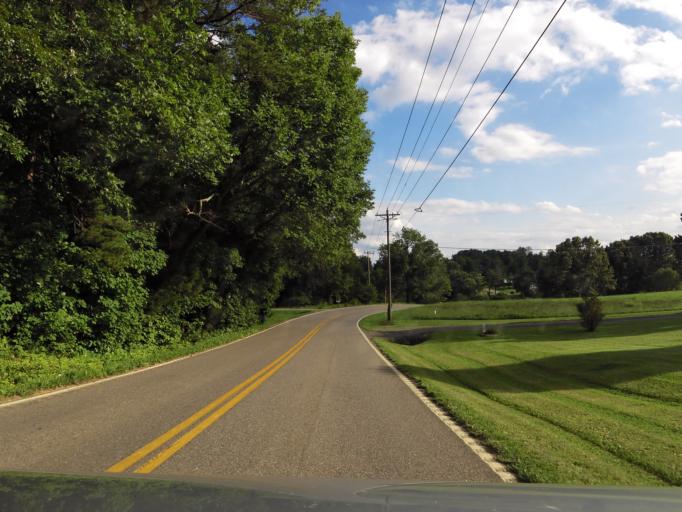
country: US
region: Tennessee
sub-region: Loudon County
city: Greenback
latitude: 35.6328
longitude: -84.0995
